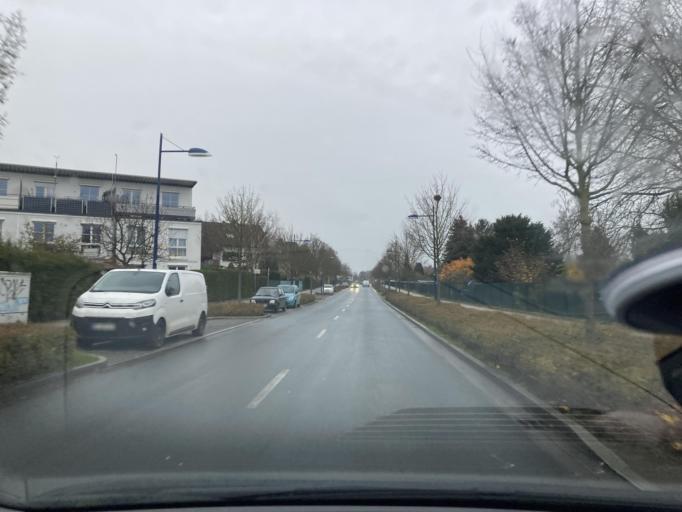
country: DE
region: Hesse
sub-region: Regierungsbezirk Darmstadt
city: Offenbach
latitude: 50.1138
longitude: 8.7887
